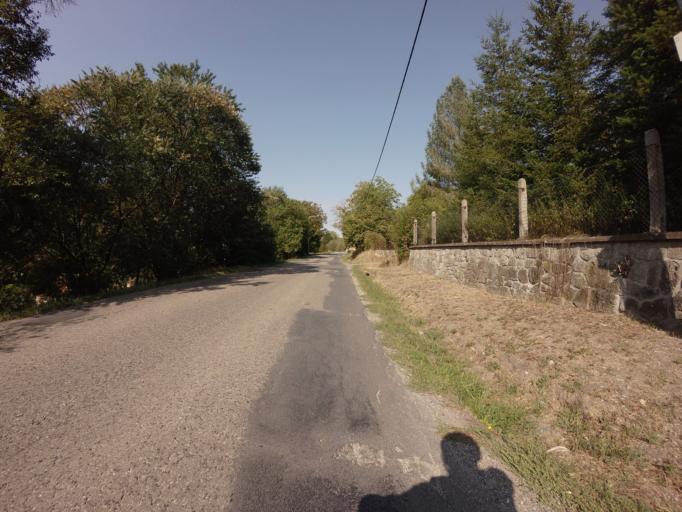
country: CZ
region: Central Bohemia
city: Tynec nad Sazavou
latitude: 49.8402
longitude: 14.5677
